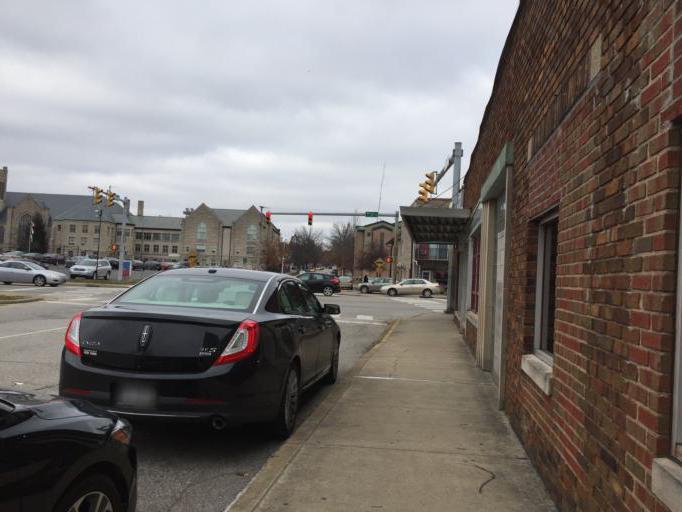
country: US
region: Indiana
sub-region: Monroe County
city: Bloomington
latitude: 39.1643
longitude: -86.5311
